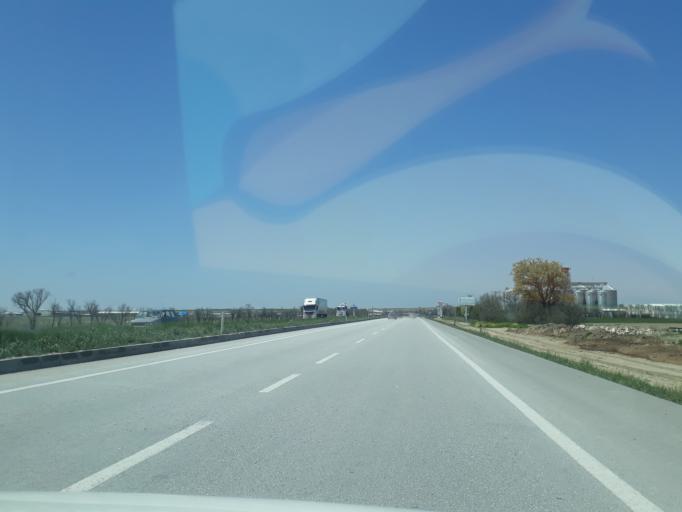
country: TR
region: Konya
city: Karapinar
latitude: 37.7153
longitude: 33.5079
